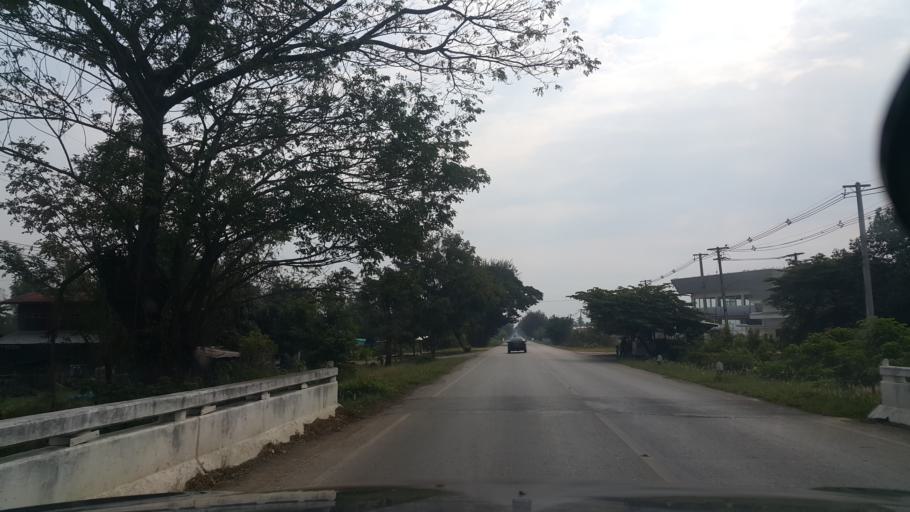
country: TH
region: Sukhothai
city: Si Samrong
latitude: 17.1816
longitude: 99.8354
